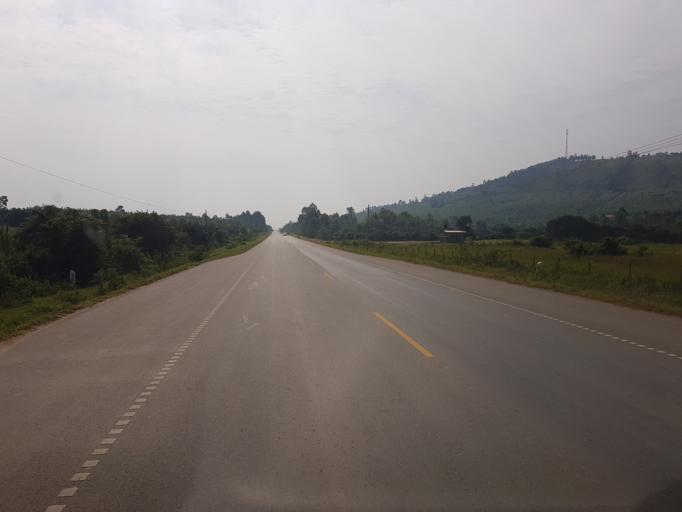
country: UG
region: Western Region
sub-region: Sheema District
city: Kibingo
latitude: -0.6408
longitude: 30.5063
